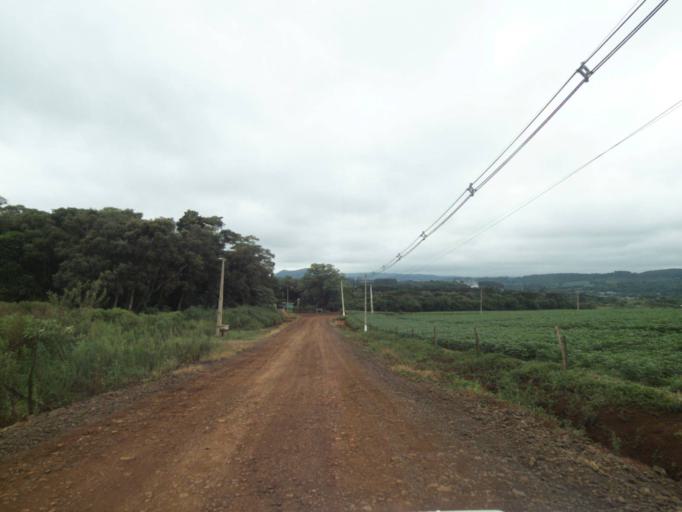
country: BR
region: Parana
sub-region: Pitanga
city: Pitanga
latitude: -24.9421
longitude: -51.8797
